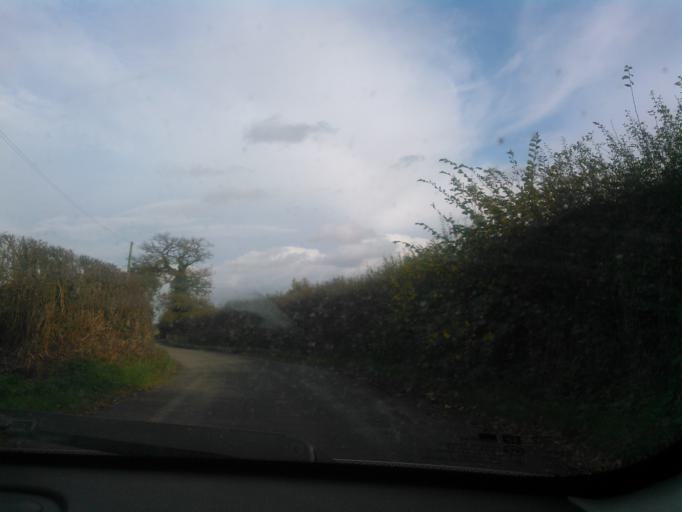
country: GB
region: England
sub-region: Shropshire
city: Wem
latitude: 52.8520
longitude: -2.7011
